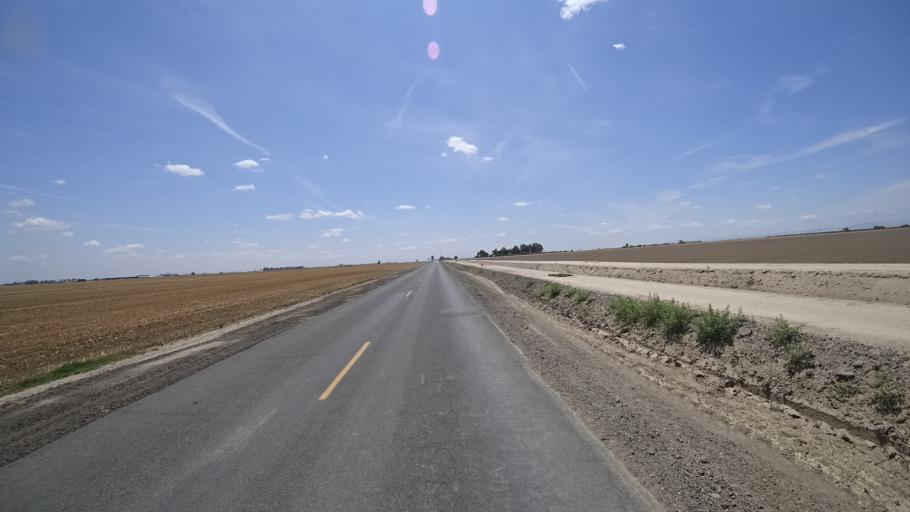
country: US
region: California
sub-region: Kings County
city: Home Garden
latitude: 36.2458
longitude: -119.6728
